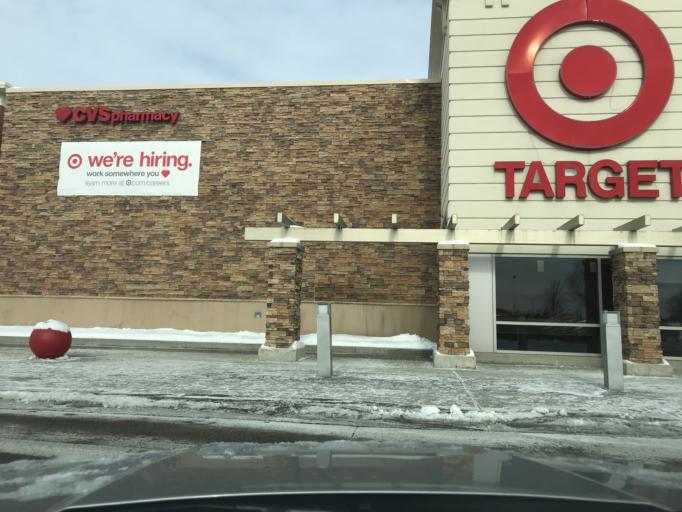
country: US
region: Wisconsin
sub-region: Dane County
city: Sun Prairie
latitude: 43.1706
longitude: -89.2676
